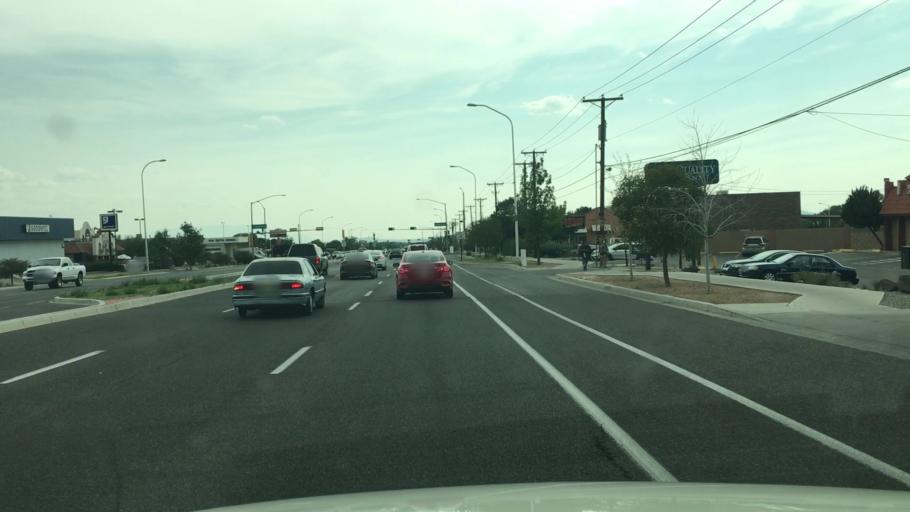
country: US
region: New Mexico
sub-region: Santa Fe County
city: Agua Fria
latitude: 35.6544
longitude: -105.9935
